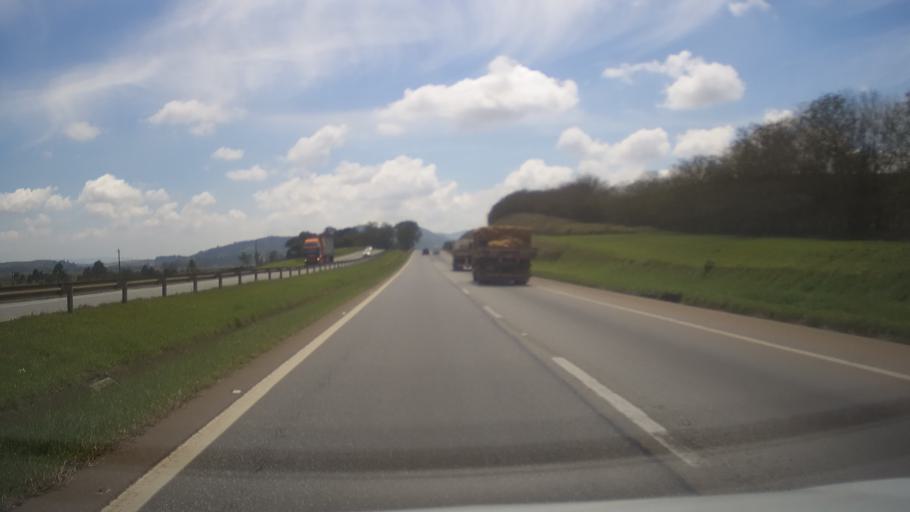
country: BR
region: Minas Gerais
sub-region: Santa Rita Do Sapucai
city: Santa Rita do Sapucai
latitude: -22.1015
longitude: -45.7225
